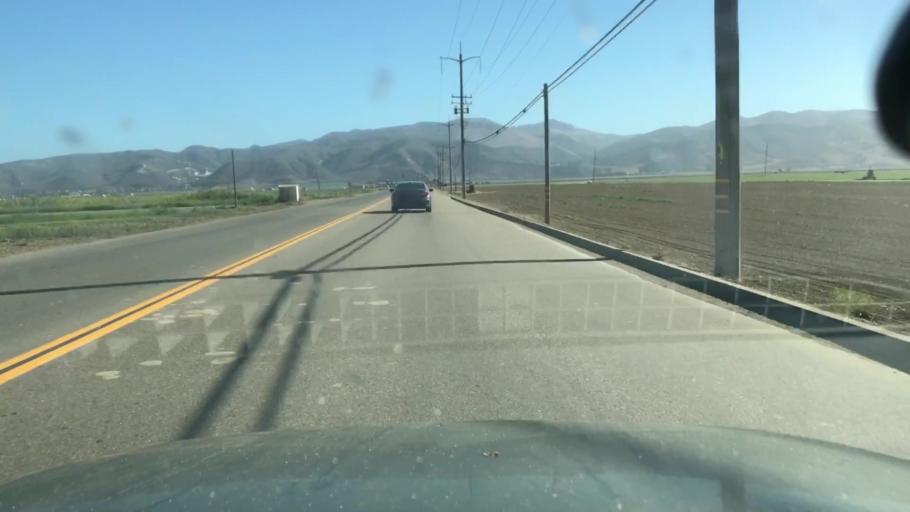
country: US
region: California
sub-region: Santa Barbara County
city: Lompoc
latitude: 34.6664
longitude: -120.4934
